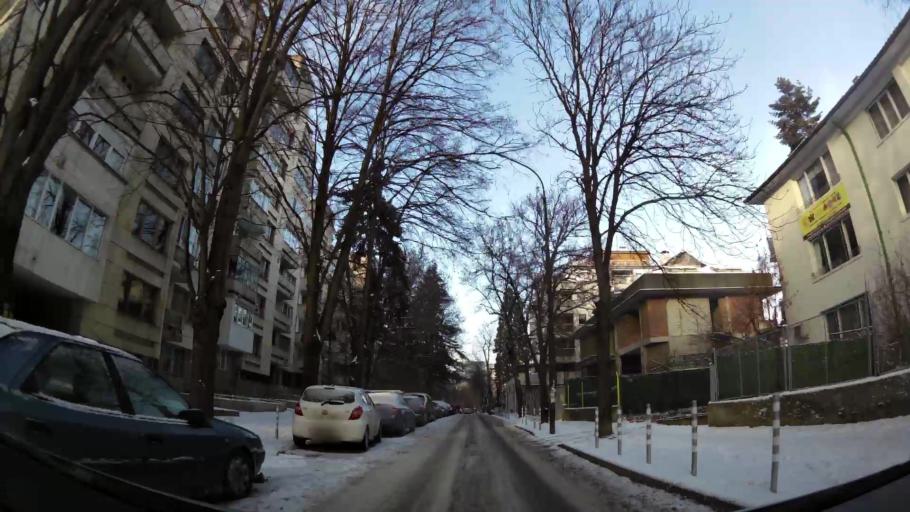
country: BG
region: Sofia-Capital
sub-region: Stolichna Obshtina
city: Sofia
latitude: 42.6716
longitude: 23.3306
